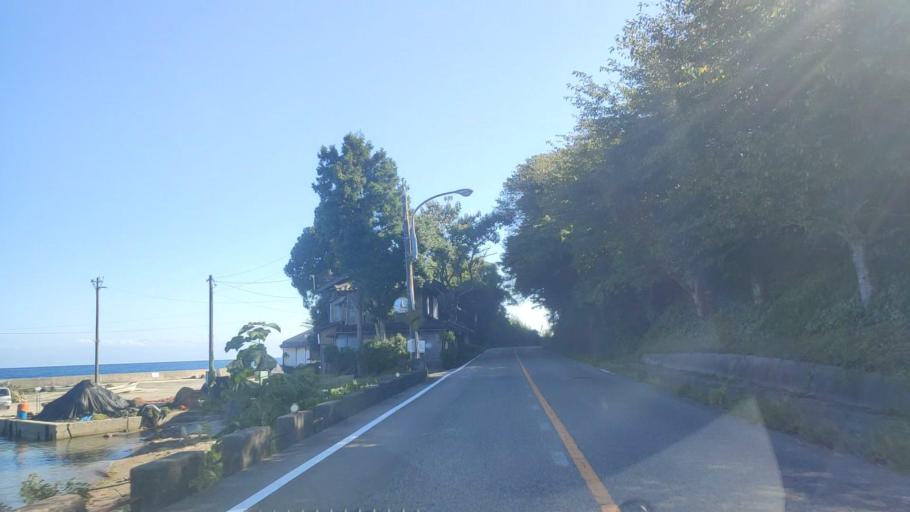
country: JP
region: Ishikawa
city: Nanao
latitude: 37.2743
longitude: 137.0969
